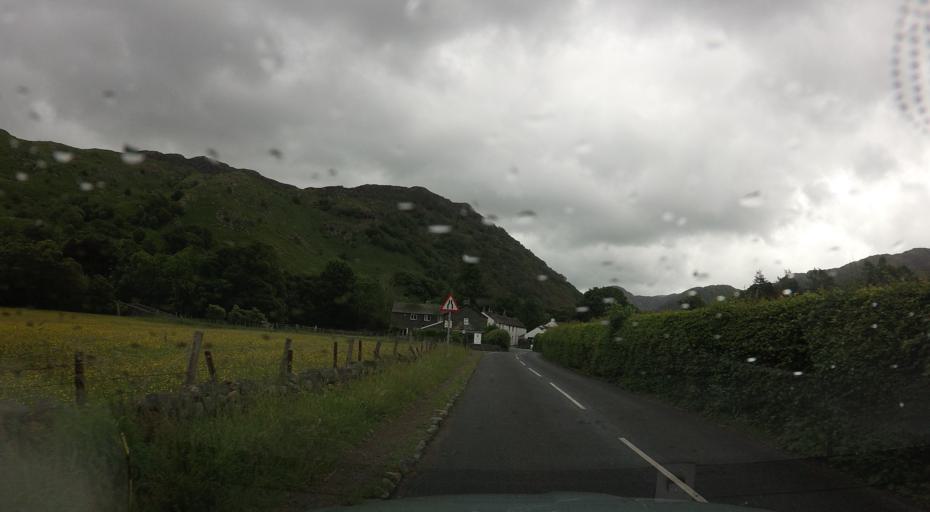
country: GB
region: England
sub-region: Cumbria
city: Keswick
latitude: 54.5245
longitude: -3.1482
